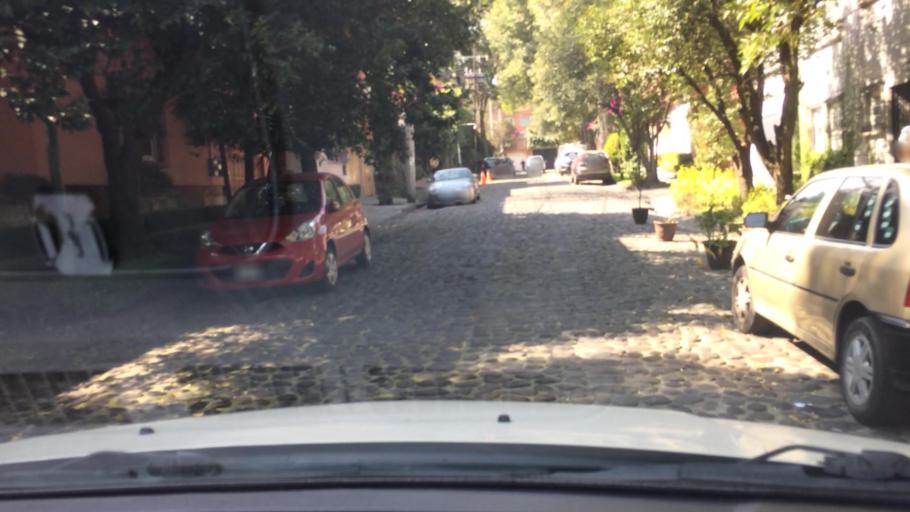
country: MX
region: Mexico City
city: Alvaro Obregon
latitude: 19.3505
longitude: -99.1973
